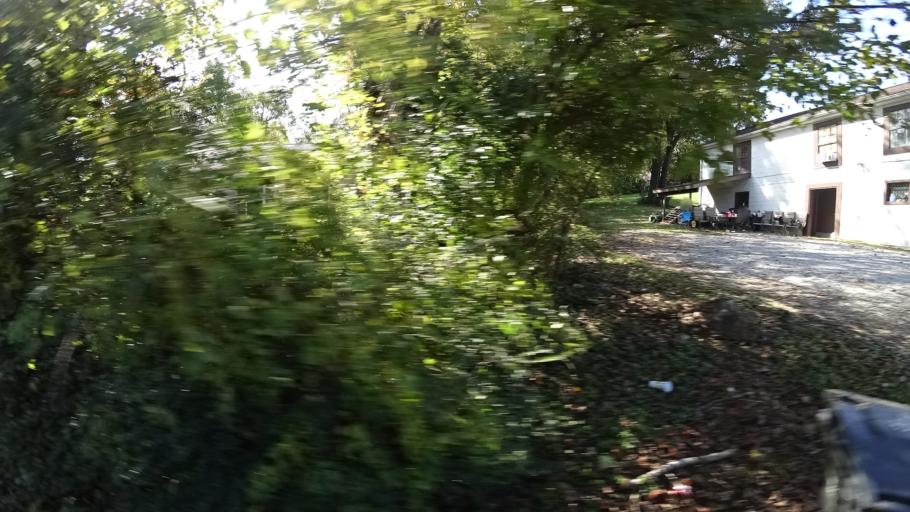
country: US
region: Tennessee
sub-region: Knox County
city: Knoxville
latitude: 35.9515
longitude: -83.9761
